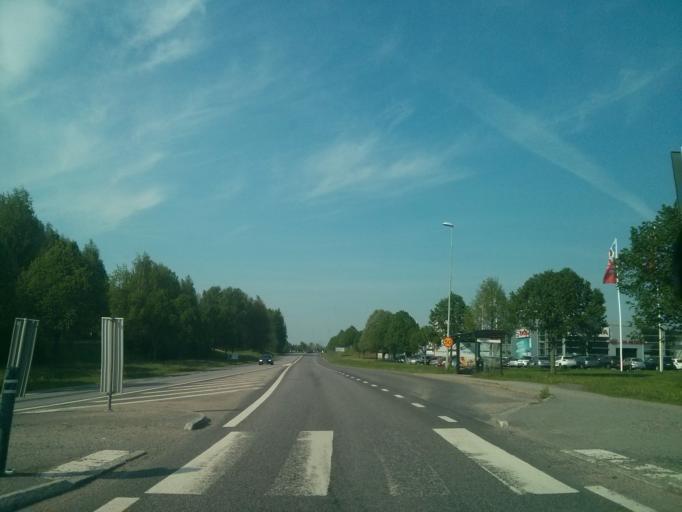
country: SE
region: Soedermanland
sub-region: Katrineholms Kommun
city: Katrineholm
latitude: 58.9984
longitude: 16.2201
